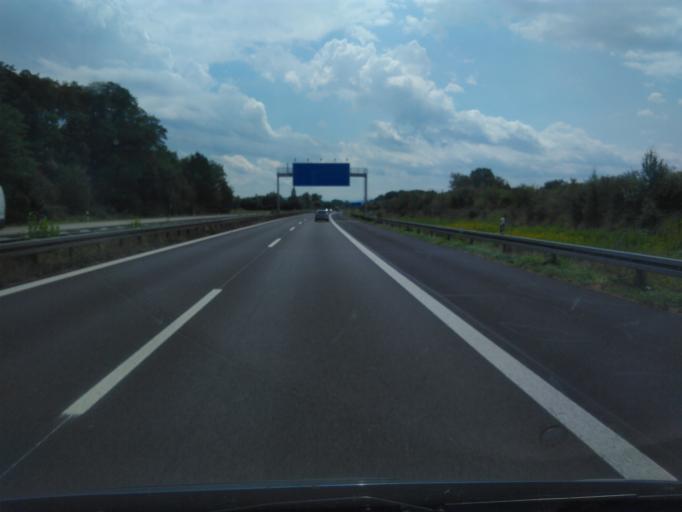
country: DE
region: Baden-Wuerttemberg
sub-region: Freiburg Region
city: Efringen-Kirchen
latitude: 47.6352
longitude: 7.5671
